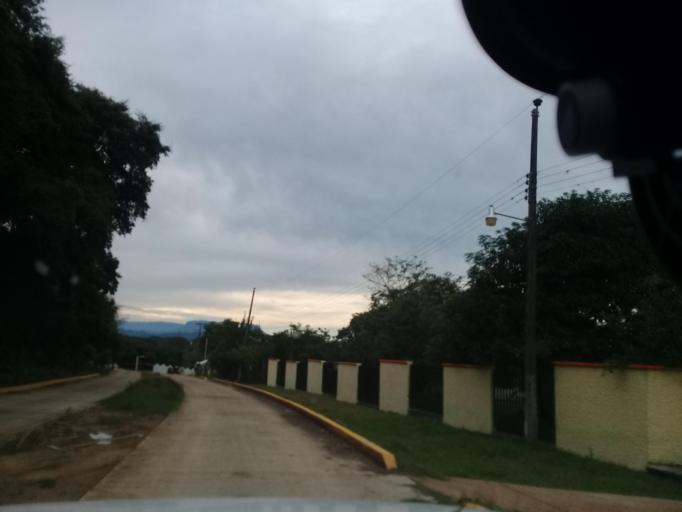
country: MX
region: Hidalgo
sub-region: Huejutla de Reyes
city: Chalahuiyapa
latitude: 21.1627
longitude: -98.3519
